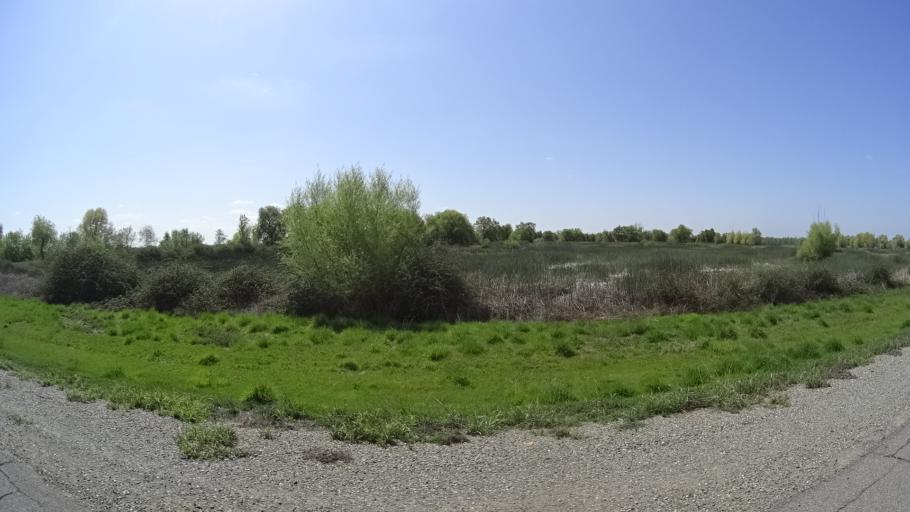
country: US
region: California
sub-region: Butte County
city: Biggs
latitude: 39.4640
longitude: -121.8720
